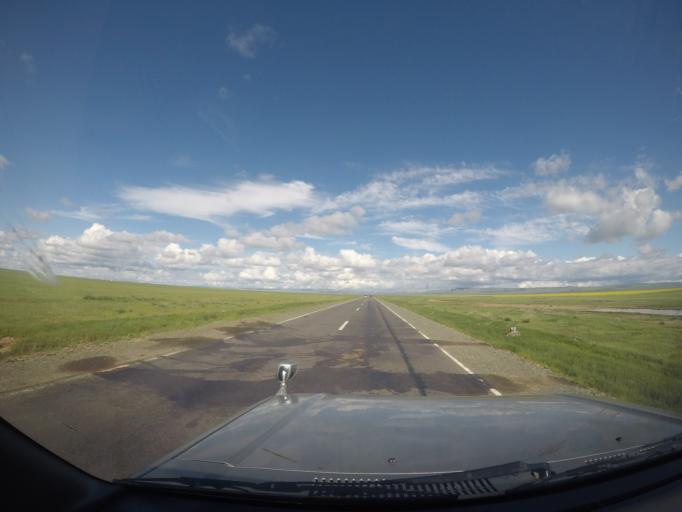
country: MN
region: Hentiy
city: Moron
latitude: 47.4179
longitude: 109.9166
